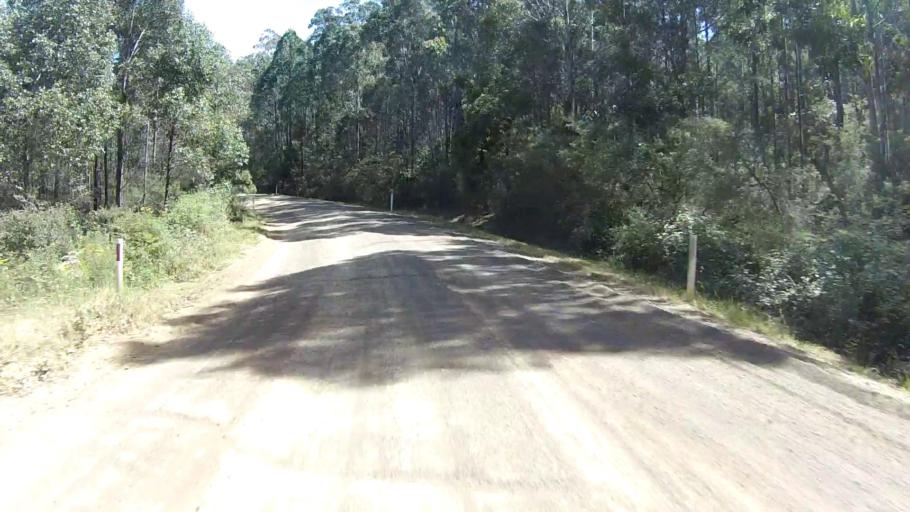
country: AU
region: Tasmania
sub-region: Sorell
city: Sorell
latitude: -42.7005
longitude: 147.7435
